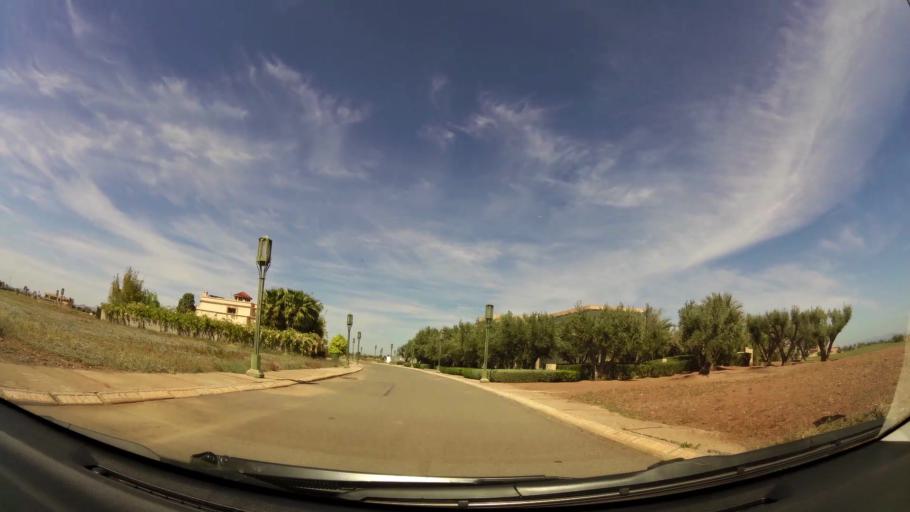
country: MA
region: Marrakech-Tensift-Al Haouz
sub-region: Marrakech
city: Marrakesh
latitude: 31.6180
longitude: -7.9244
